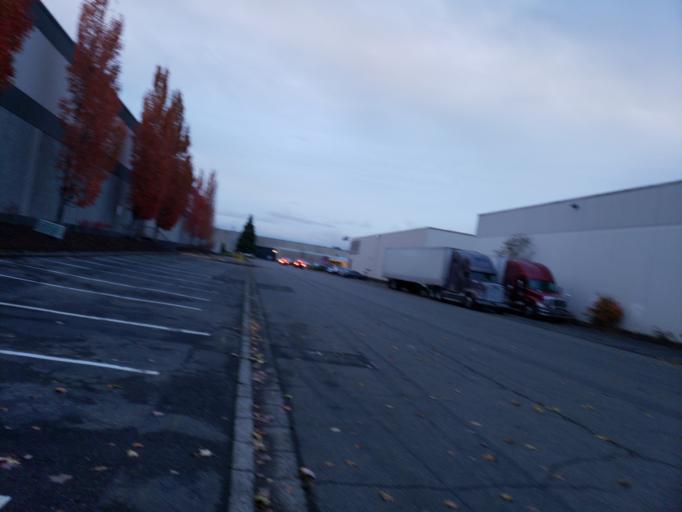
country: US
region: Washington
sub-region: King County
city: Tukwila
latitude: 47.4431
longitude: -122.2566
